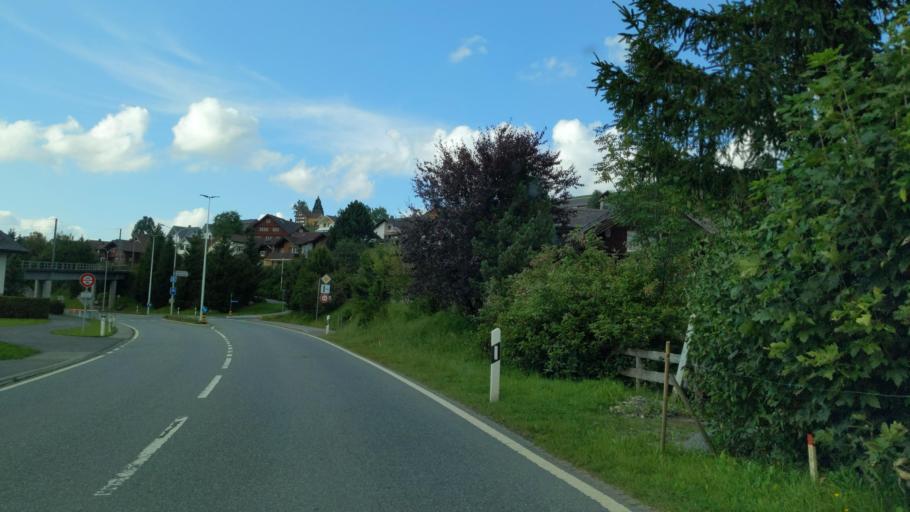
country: CH
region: Appenzell Innerrhoden
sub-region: Appenzell Inner Rhodes
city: Appenzell
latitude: 47.3293
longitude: 9.4267
